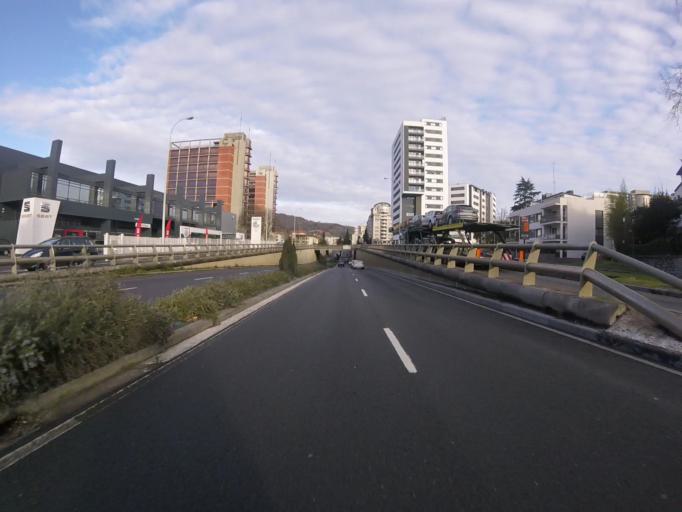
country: ES
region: Basque Country
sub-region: Provincia de Guipuzcoa
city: San Sebastian
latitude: 43.3003
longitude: -2.0019
